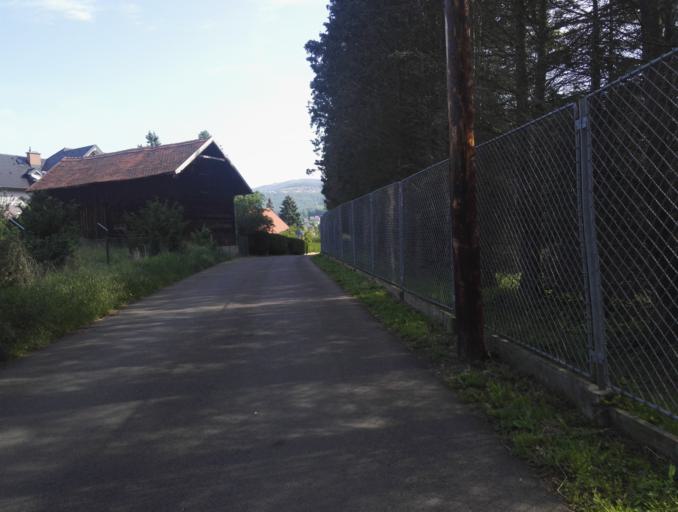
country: AT
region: Styria
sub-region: Politischer Bezirk Graz-Umgebung
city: Stattegg
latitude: 47.1142
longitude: 15.4257
